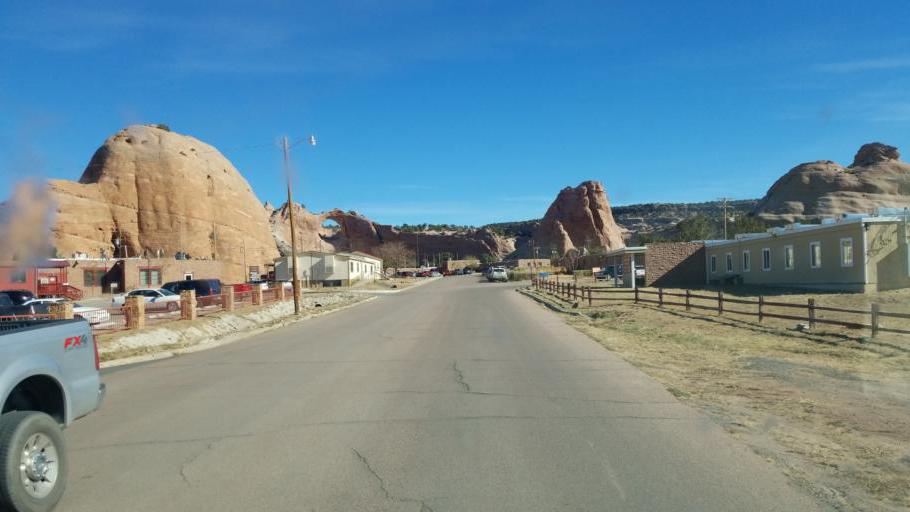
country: US
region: Arizona
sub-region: Apache County
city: Window Rock
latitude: 35.6779
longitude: -109.0516
